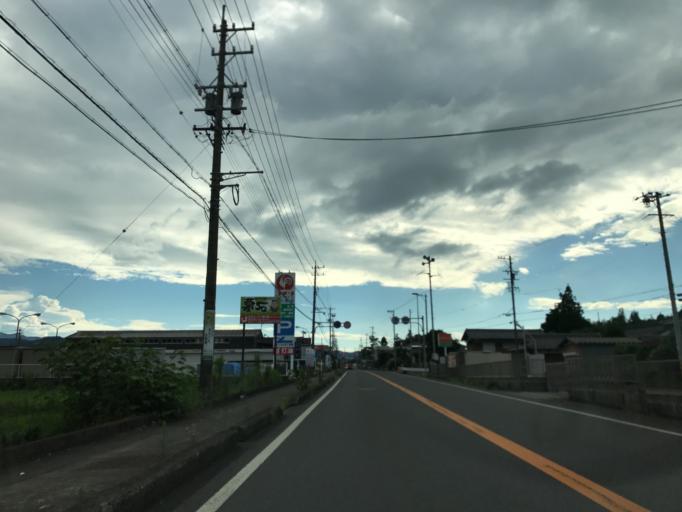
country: JP
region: Gifu
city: Tarui
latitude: 35.3646
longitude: 136.4817
